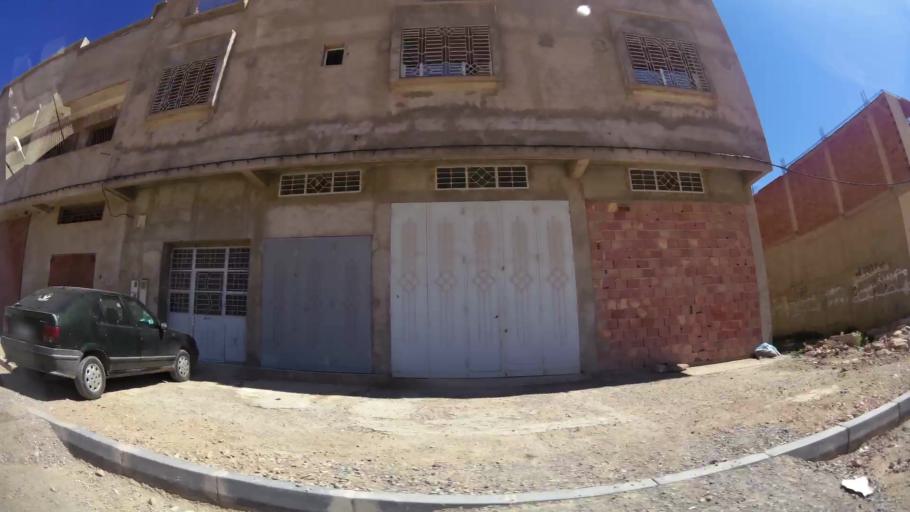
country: MA
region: Oriental
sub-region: Oujda-Angad
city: Oujda
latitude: 34.6624
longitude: -1.8693
